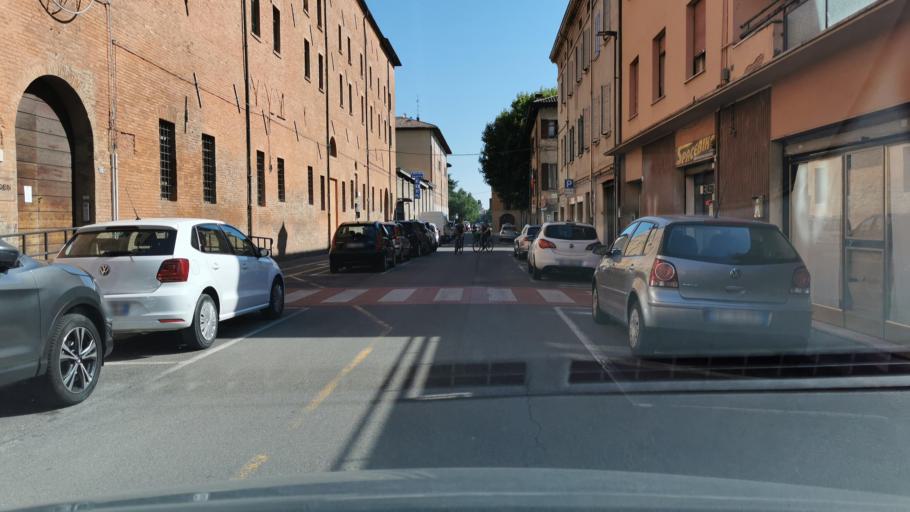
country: IT
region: Emilia-Romagna
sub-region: Provincia di Modena
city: Carpi Centro
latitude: 44.7857
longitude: 10.8842
